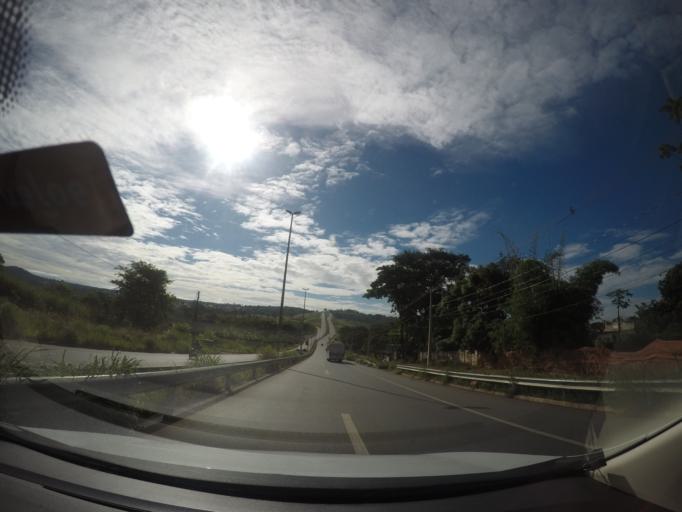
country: BR
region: Goias
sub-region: Goiania
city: Goiania
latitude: -16.6850
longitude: -49.1911
